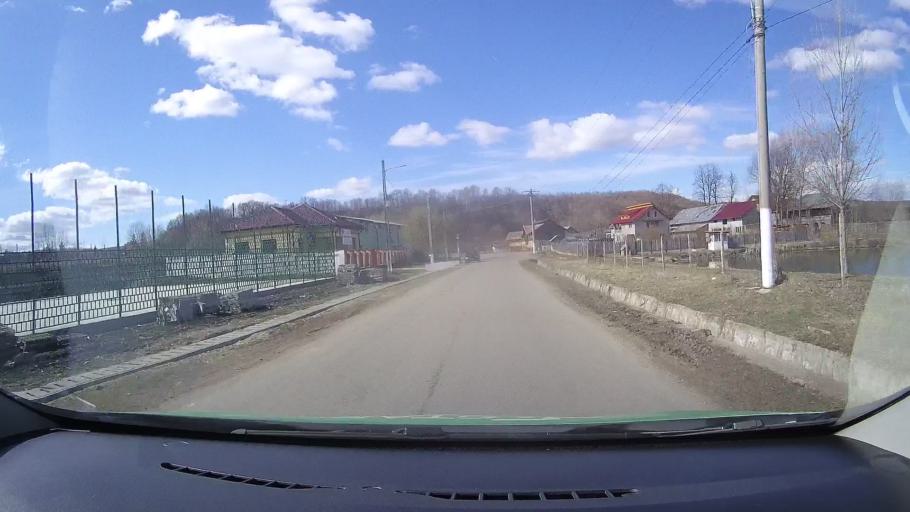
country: RO
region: Dambovita
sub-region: Comuna Sotanga
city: Sotanga
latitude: 44.9965
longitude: 25.3824
